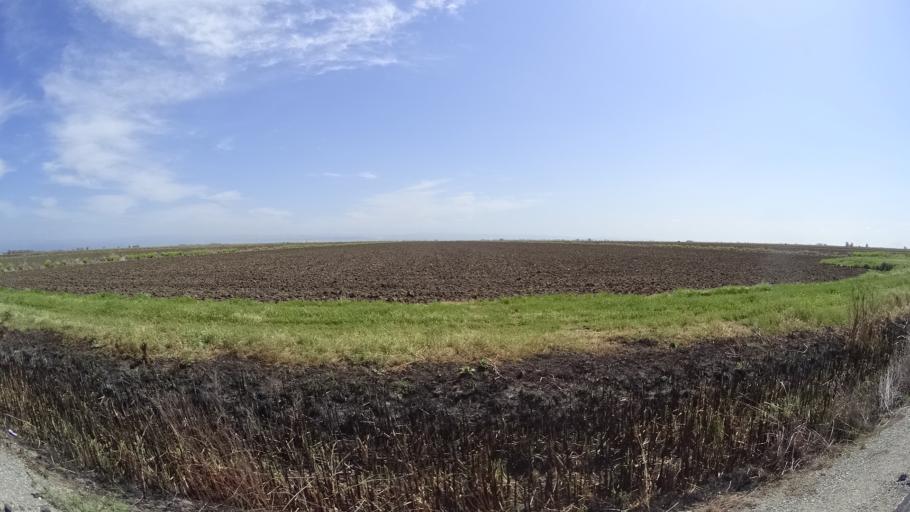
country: US
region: California
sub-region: Butte County
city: Durham
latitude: 39.5129
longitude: -121.8574
